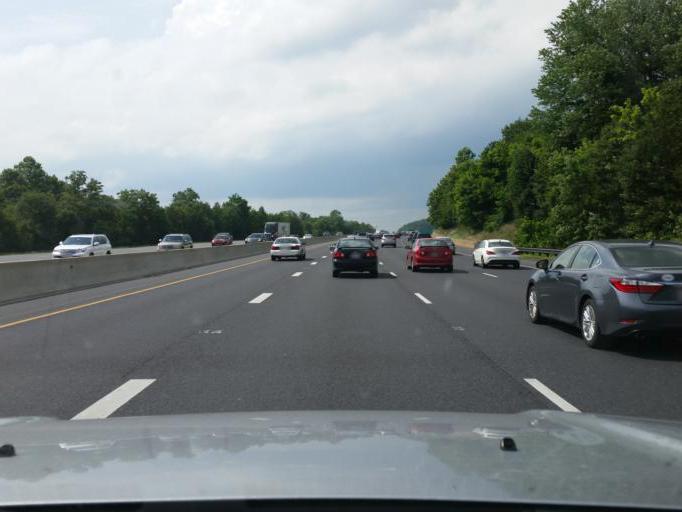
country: US
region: Maryland
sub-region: Montgomery County
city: Germantown
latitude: 39.1671
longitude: -77.2415
